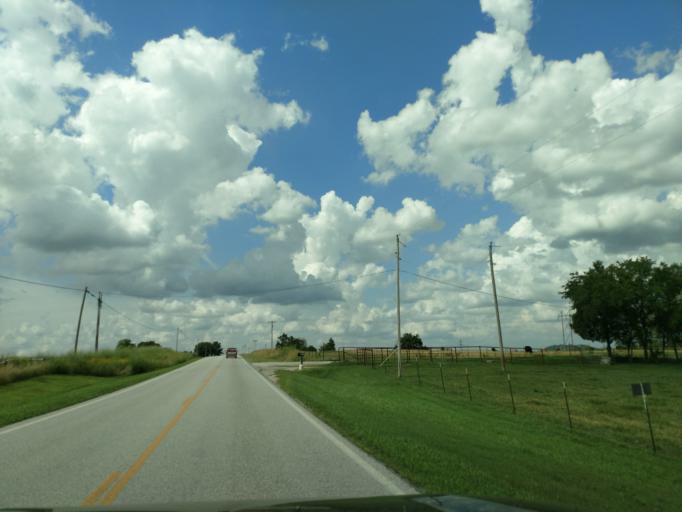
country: US
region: Arkansas
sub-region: Carroll County
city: Berryville
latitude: 36.4543
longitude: -93.5560
